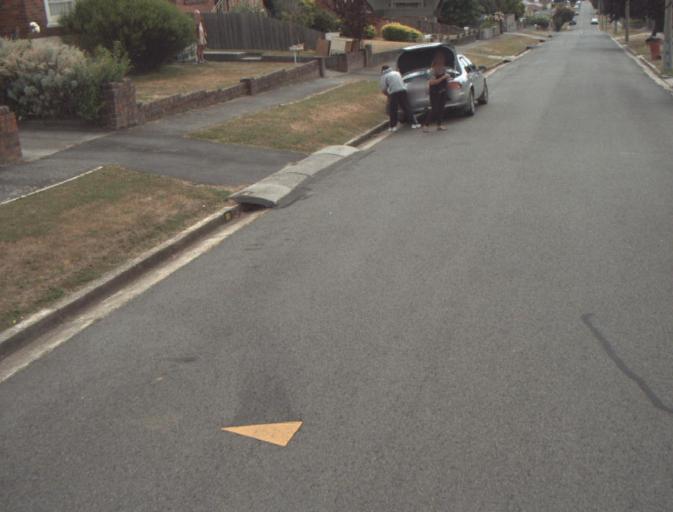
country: AU
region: Tasmania
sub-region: Launceston
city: Summerhill
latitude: -41.4701
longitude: 147.1546
